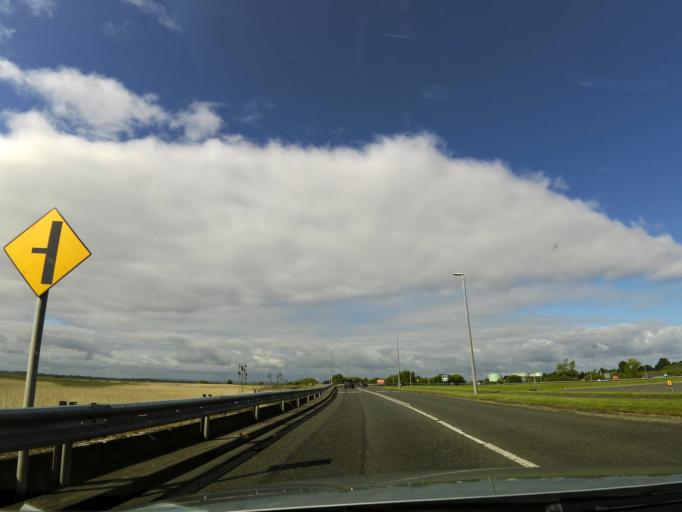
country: IE
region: Munster
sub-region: An Clar
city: Shannon
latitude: 52.6899
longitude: -8.9219
